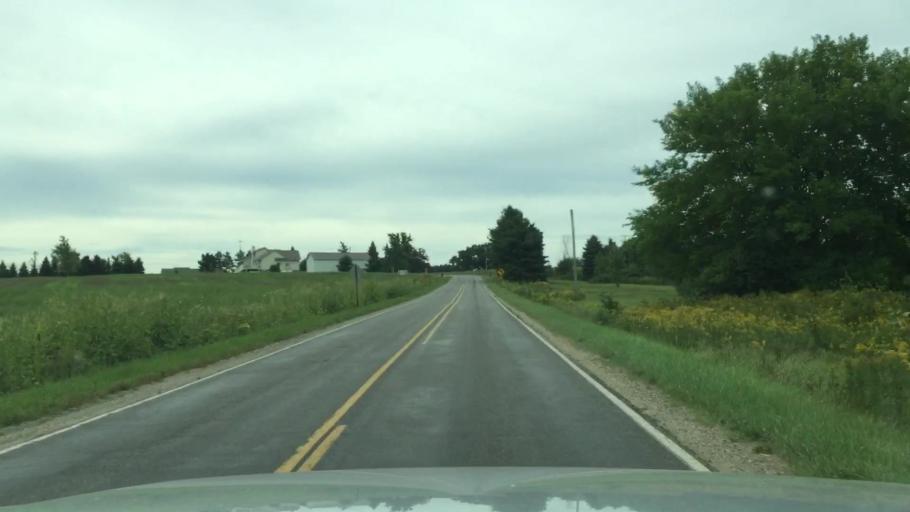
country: US
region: Michigan
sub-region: Shiawassee County
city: Durand
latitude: 42.9548
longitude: -83.9879
